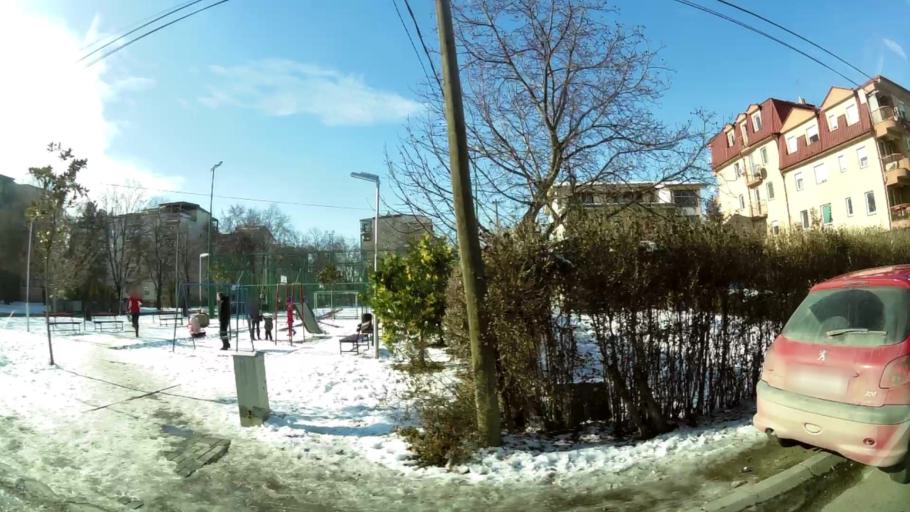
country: MK
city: Krushopek
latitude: 42.0051
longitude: 21.3549
